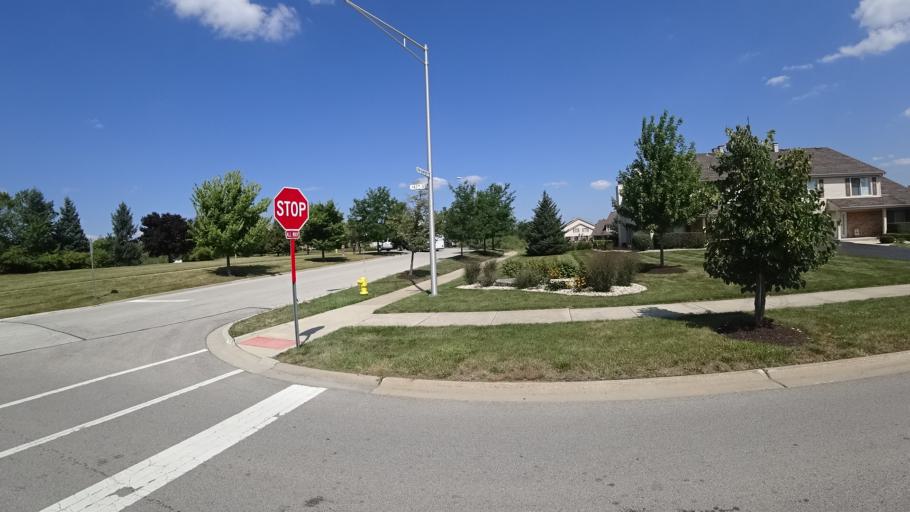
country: US
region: Illinois
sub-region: Cook County
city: Orland Park
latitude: 41.6322
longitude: -87.8488
